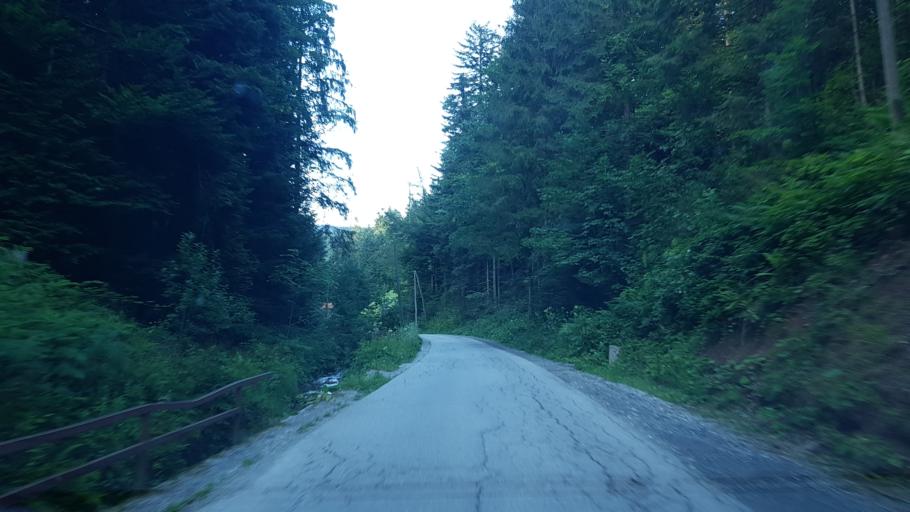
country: SI
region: Idrija
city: Spodnja Idrija
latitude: 46.0811
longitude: 14.0305
